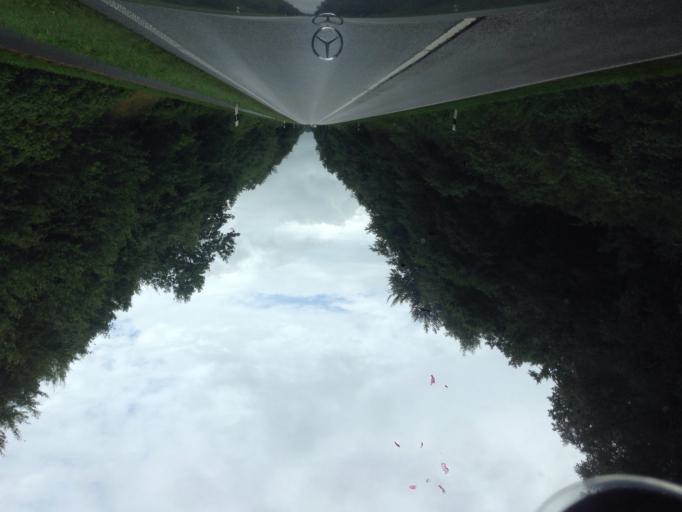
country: DE
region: Schleswig-Holstein
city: Stadum
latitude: 54.7458
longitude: 9.0281
